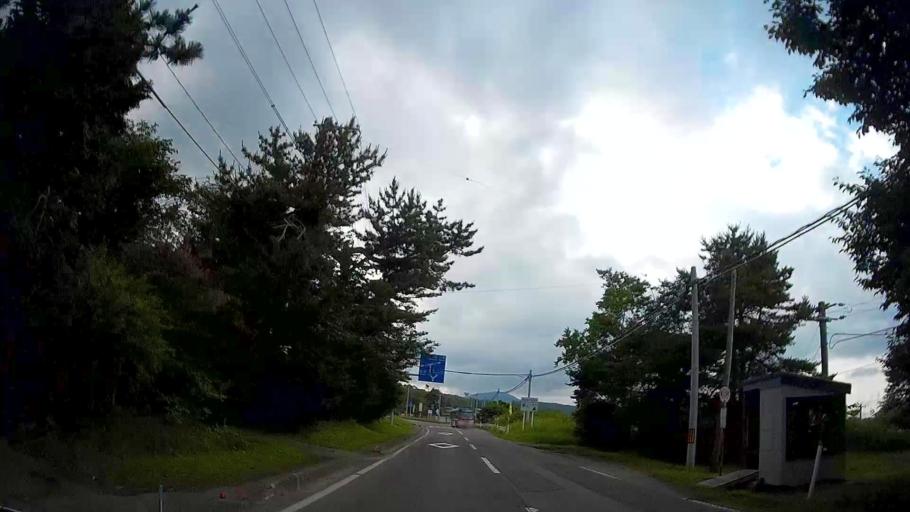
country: JP
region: Hokkaido
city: Nanae
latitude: 42.1123
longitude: 140.5522
